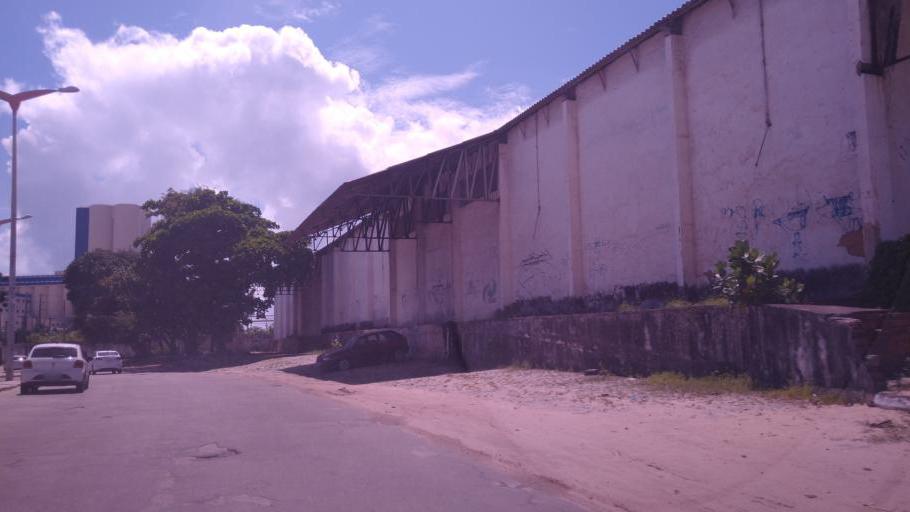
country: BR
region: Ceara
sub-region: Fortaleza
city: Fortaleza
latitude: -3.7188
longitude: -38.4751
